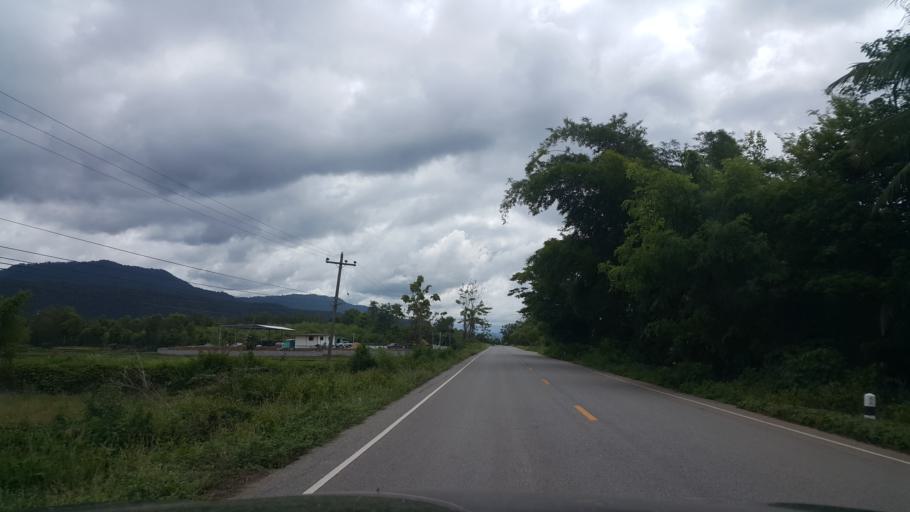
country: TH
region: Phitsanulok
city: Chat Trakan
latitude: 17.2917
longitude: 100.6477
